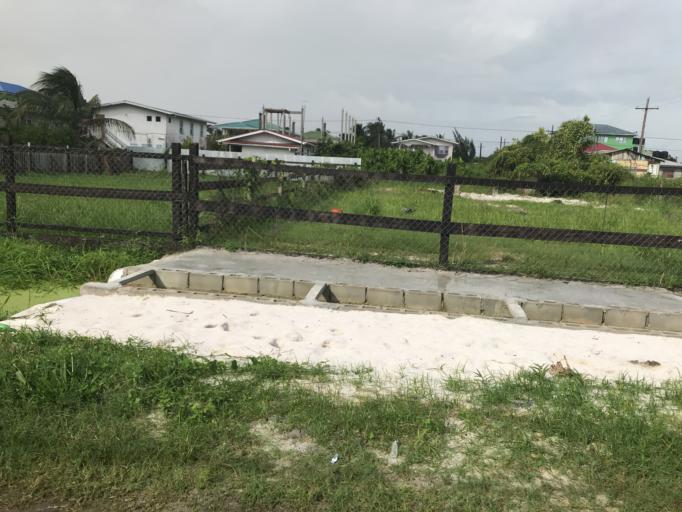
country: GY
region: Demerara-Mahaica
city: Georgetown
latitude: 6.8022
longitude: -58.1220
